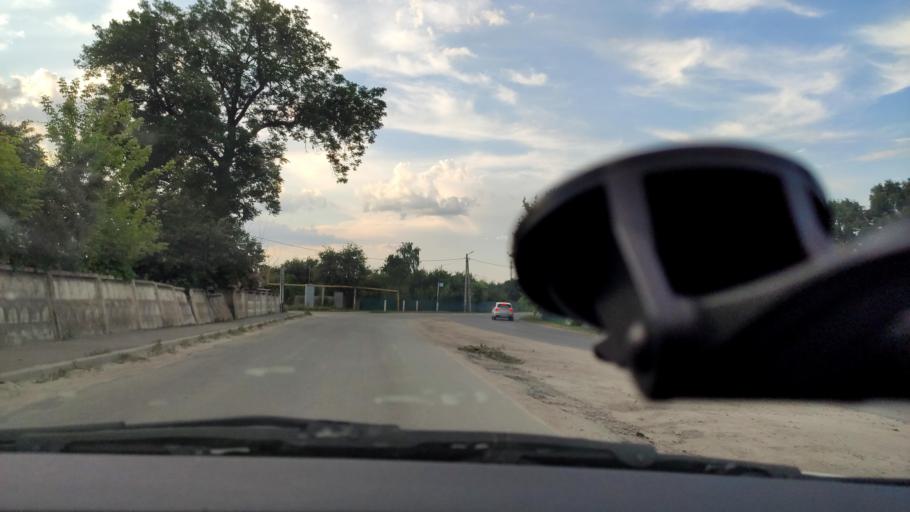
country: RU
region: Voronezj
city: Ramon'
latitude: 51.9046
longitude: 39.3327
